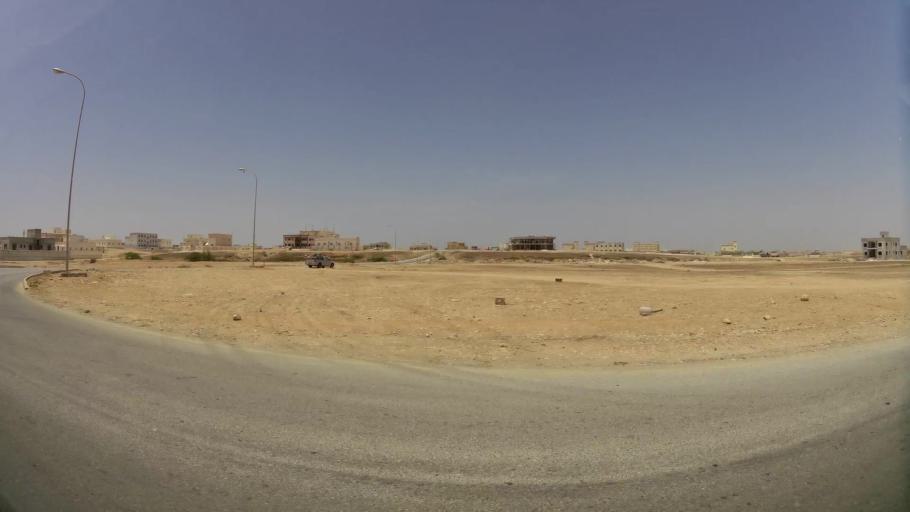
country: OM
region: Zufar
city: Salalah
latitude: 17.0917
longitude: 54.1975
